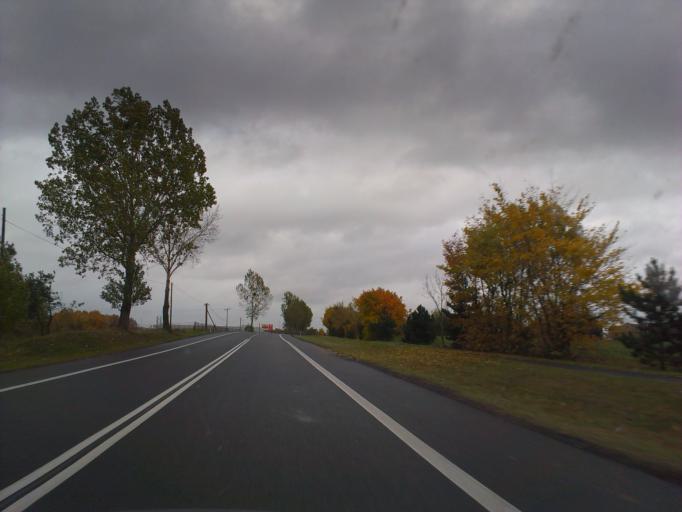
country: PL
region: Kujawsko-Pomorskie
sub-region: Powiat chelminski
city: Chelmno
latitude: 53.3311
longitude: 18.4845
